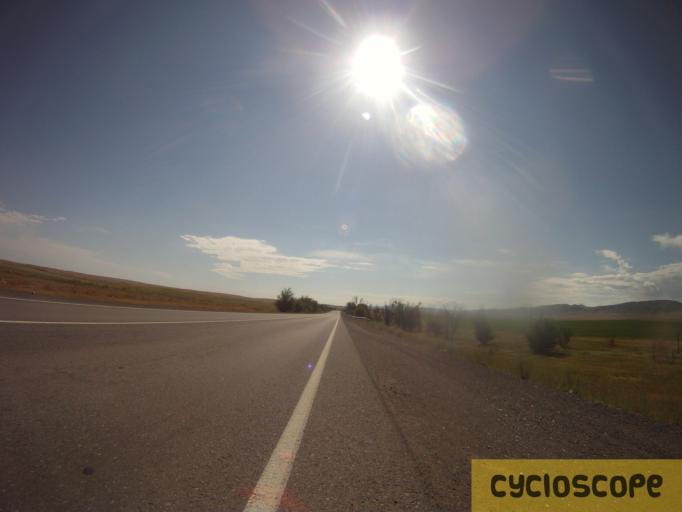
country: KG
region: Chuy
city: Bystrovka
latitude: 43.3183
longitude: 75.7510
